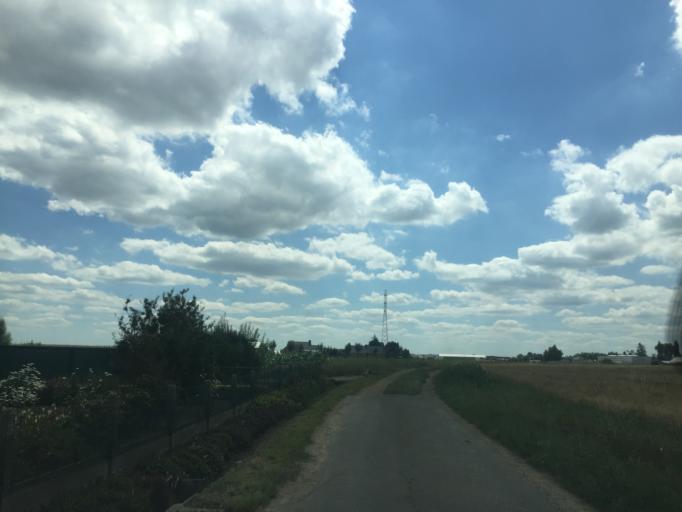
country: BE
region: Flanders
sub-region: Provincie West-Vlaanderen
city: Staden
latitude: 50.9603
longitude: 3.0300
